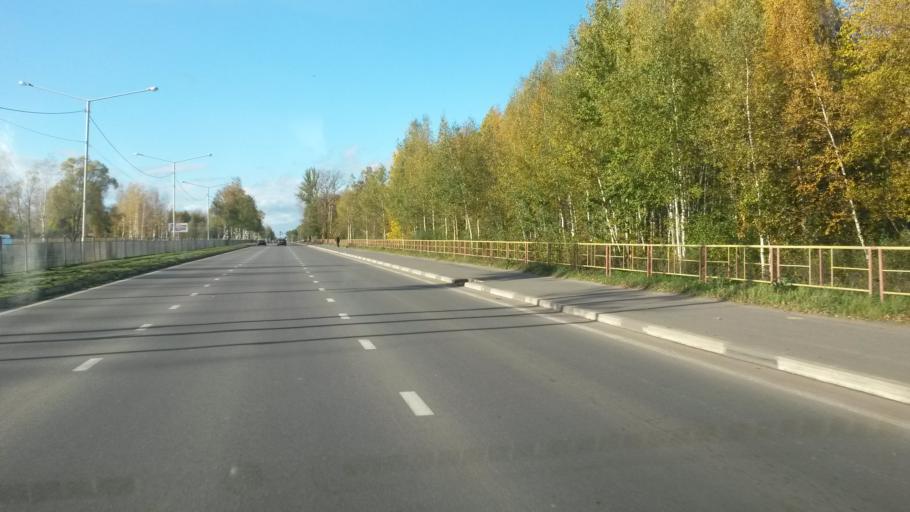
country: RU
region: Jaroslavl
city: Yaroslavl
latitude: 57.5575
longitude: 39.9394
